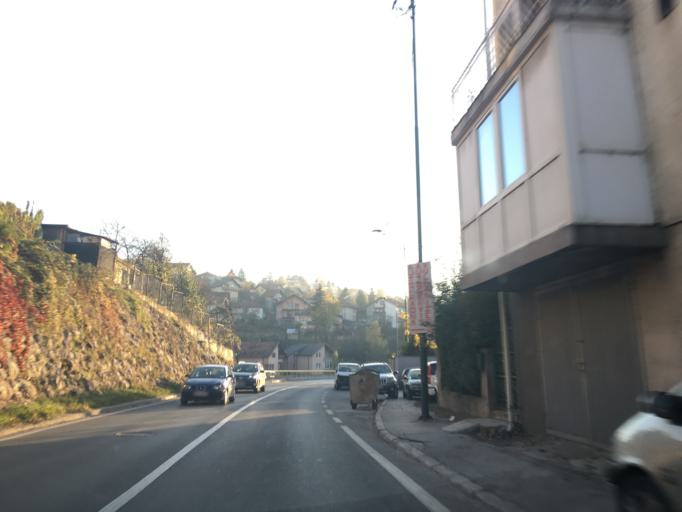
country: BA
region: Federation of Bosnia and Herzegovina
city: Kobilja Glava
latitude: 43.8488
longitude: 18.4026
